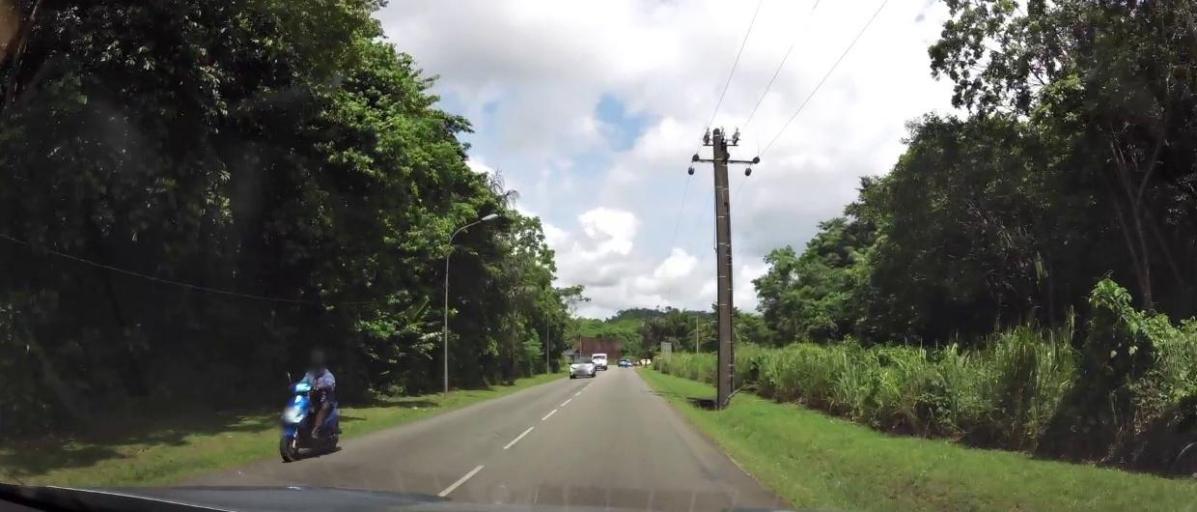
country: GF
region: Guyane
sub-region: Guyane
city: Matoury
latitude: 4.8758
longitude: -52.3358
